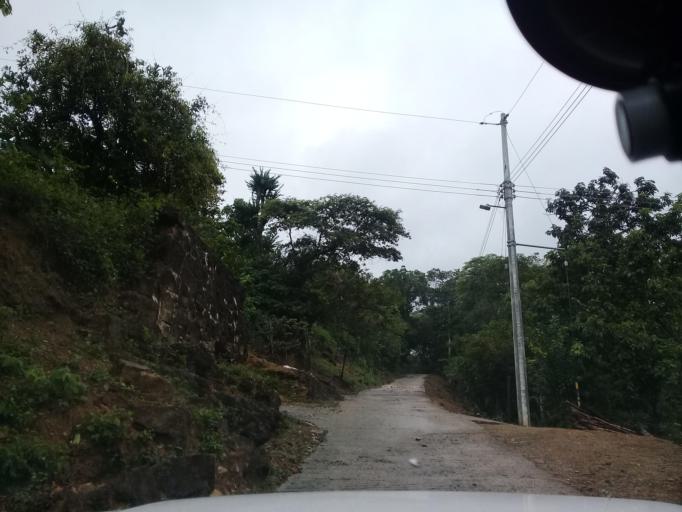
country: MX
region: Veracruz
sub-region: Chalma
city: San Pedro Coyutla
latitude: 21.2398
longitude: -98.4272
